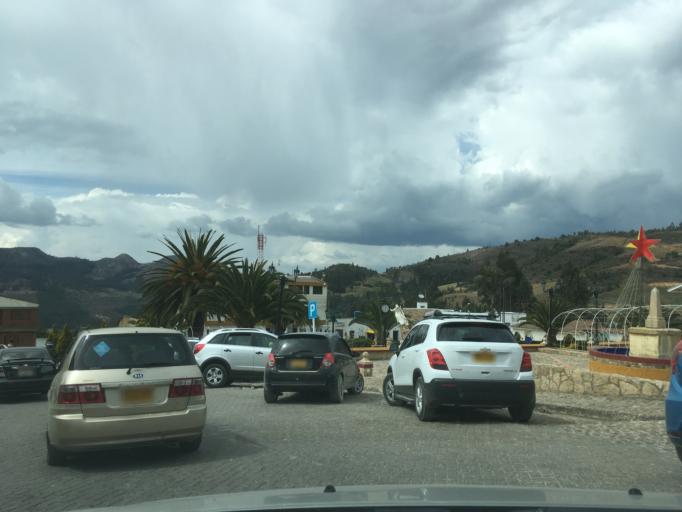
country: CO
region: Boyaca
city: Pesca
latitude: 5.5806
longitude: -72.9660
